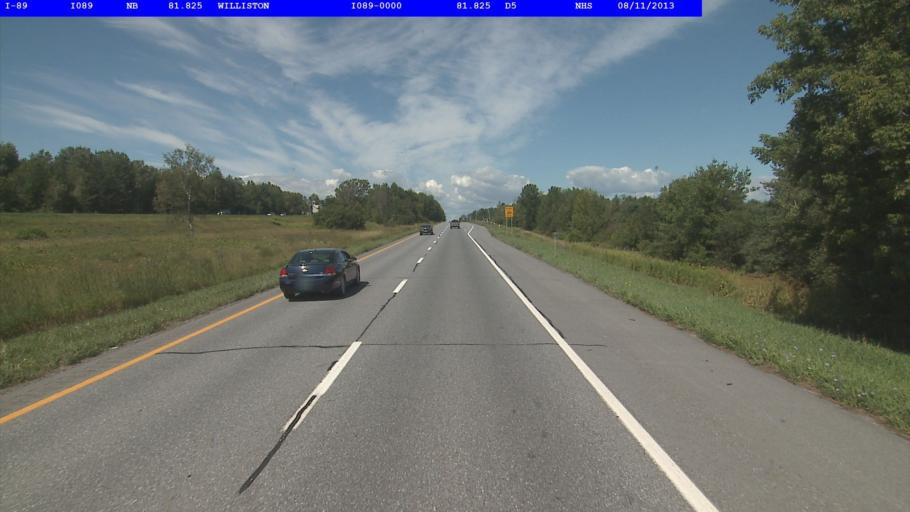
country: US
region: Vermont
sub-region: Chittenden County
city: Williston
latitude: 44.4348
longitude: -73.0724
